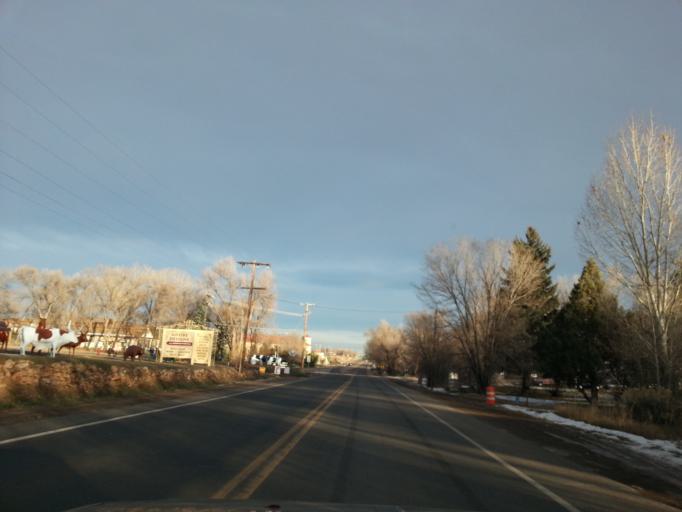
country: US
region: Colorado
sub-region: Larimer County
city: Loveland
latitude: 40.4073
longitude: -105.1358
